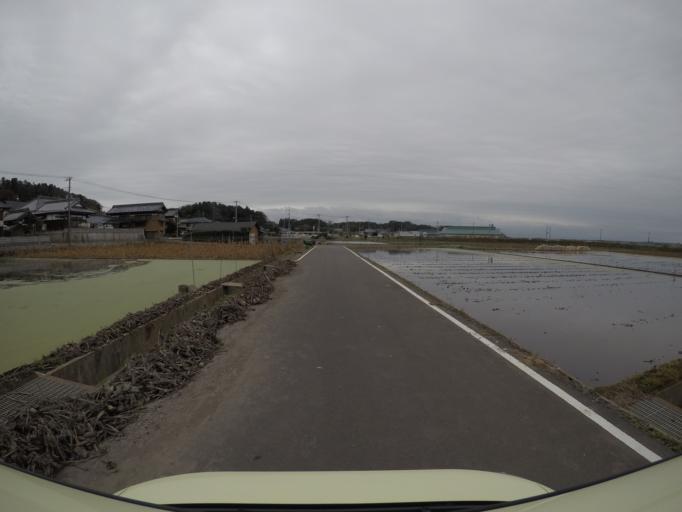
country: JP
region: Ibaraki
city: Ami
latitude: 36.0923
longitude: 140.2383
